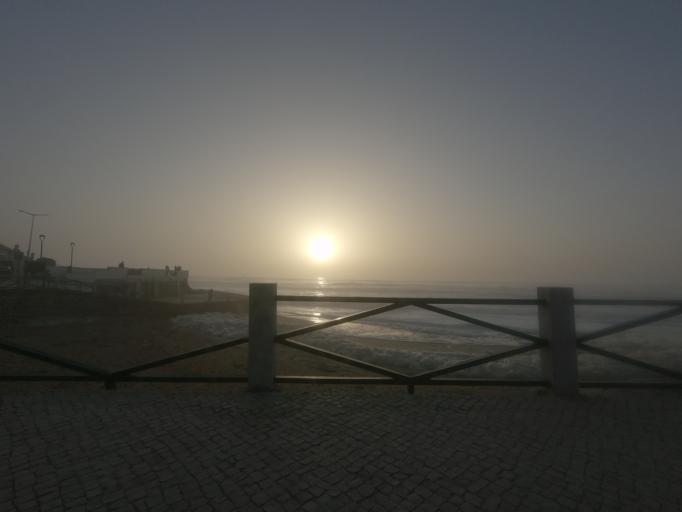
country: PT
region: Leiria
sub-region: Alcobaca
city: Pataias
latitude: 39.7561
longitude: -9.0317
